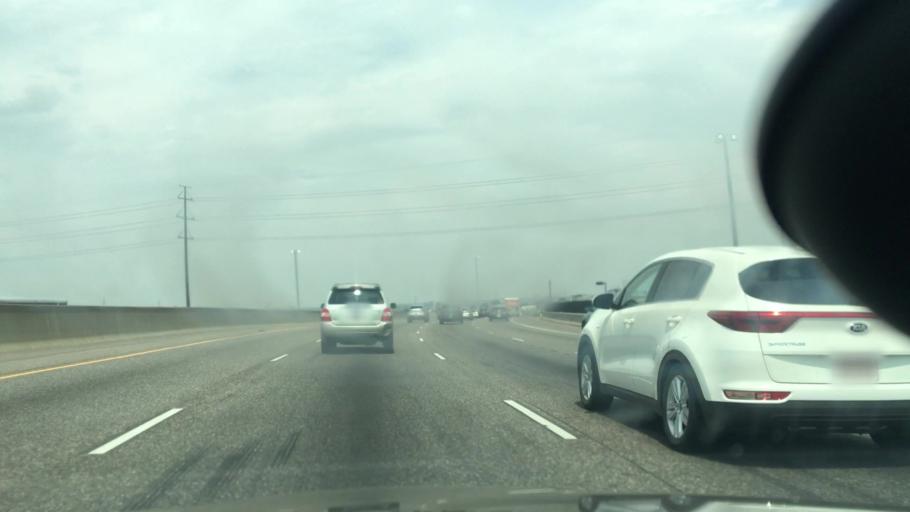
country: US
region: Colorado
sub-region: Denver County
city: Denver
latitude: 39.7052
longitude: -104.9976
